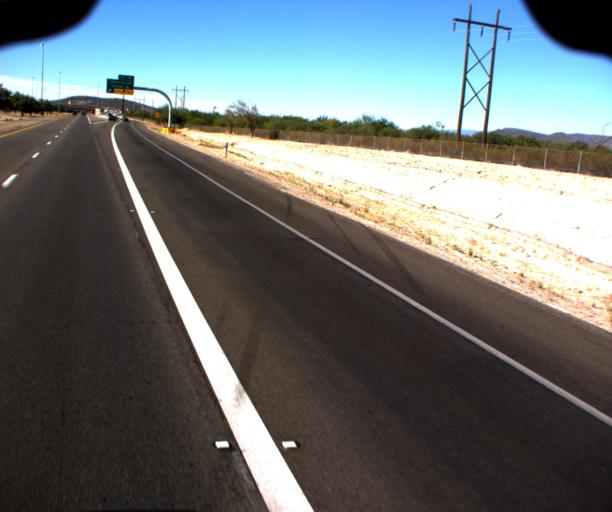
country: US
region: Arizona
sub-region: Pima County
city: Drexel Heights
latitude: 32.1416
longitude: -110.9868
